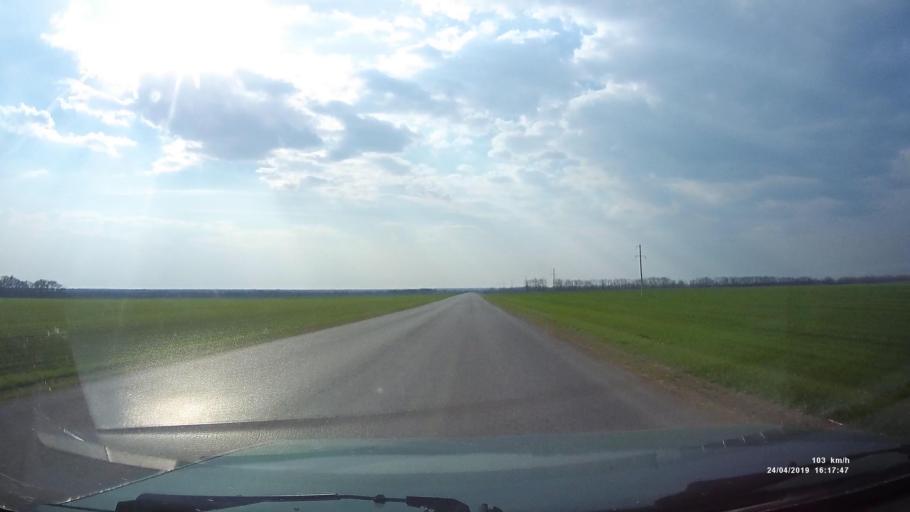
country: RU
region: Rostov
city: Sovetskoye
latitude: 46.7707
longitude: 42.1305
